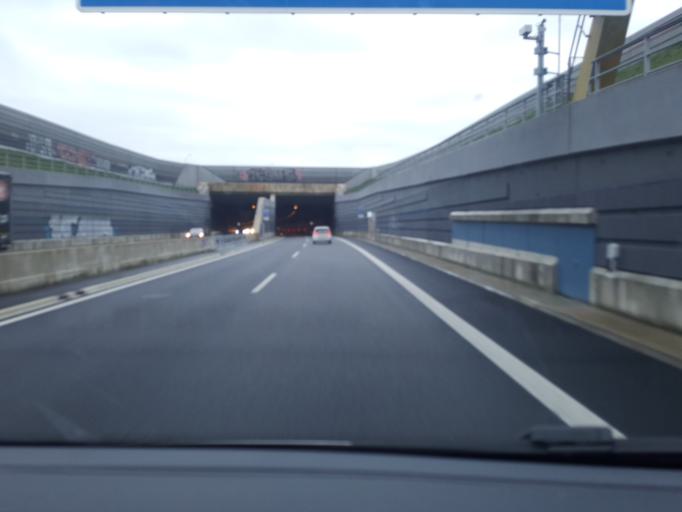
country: DE
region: North Rhine-Westphalia
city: Bad Oeynhausen
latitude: 52.2260
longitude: 8.8204
